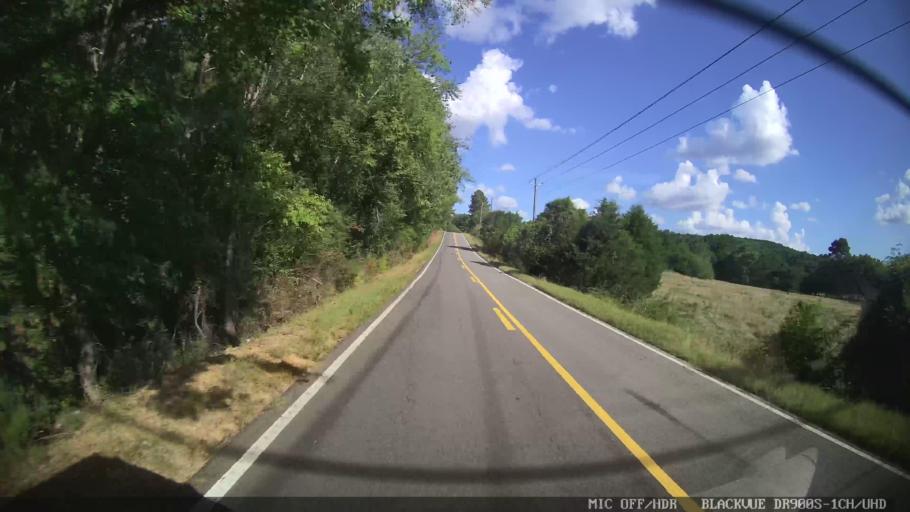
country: US
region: Georgia
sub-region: Floyd County
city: Lindale
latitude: 34.2062
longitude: -85.1193
